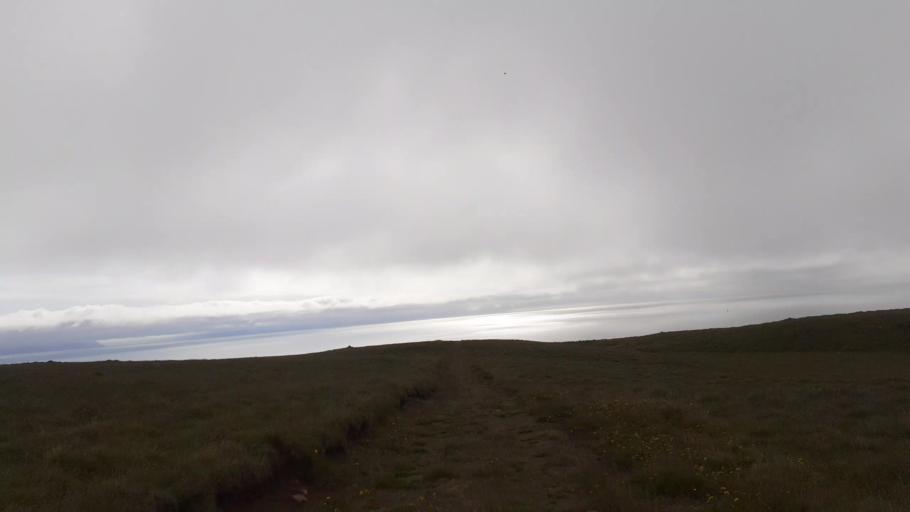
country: IS
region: Northeast
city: Dalvik
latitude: 66.5449
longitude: -17.9994
